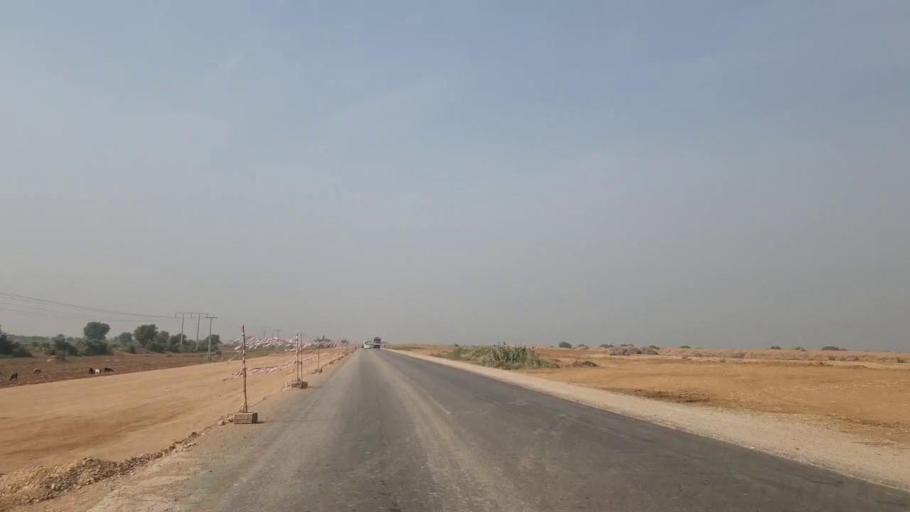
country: PK
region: Sindh
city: Sann
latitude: 26.1251
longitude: 68.0550
